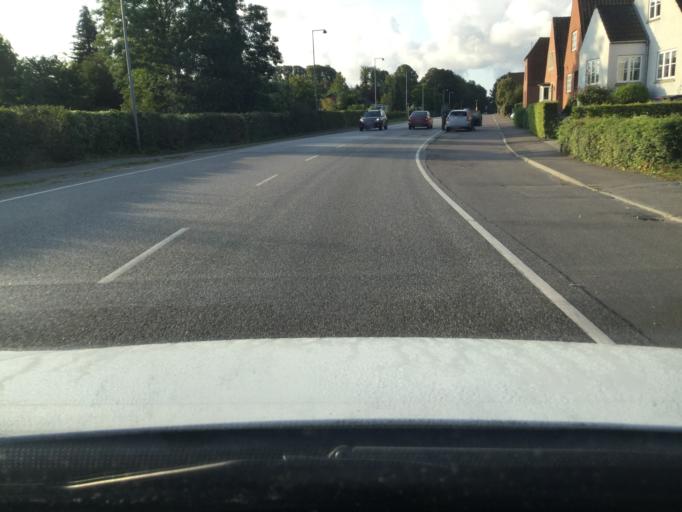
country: DK
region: Zealand
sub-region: Lolland Kommune
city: Nakskov
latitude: 54.8225
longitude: 11.1544
